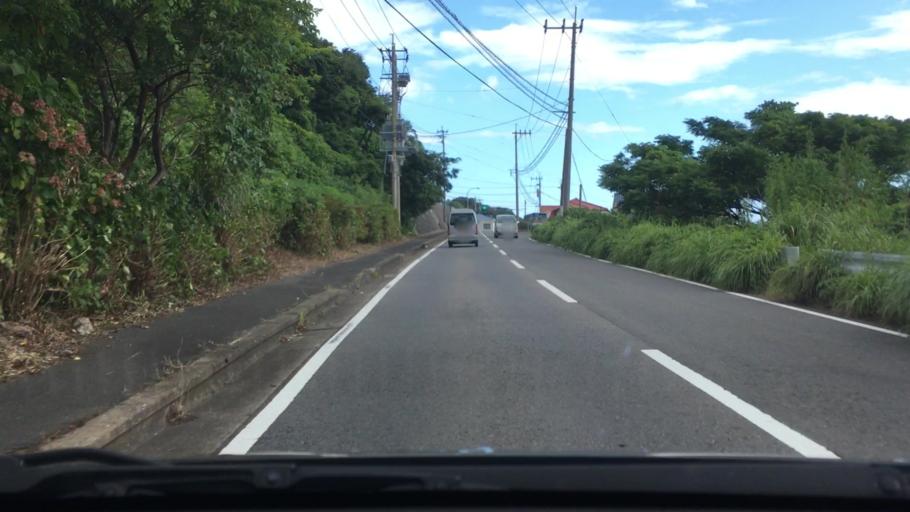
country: JP
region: Nagasaki
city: Togitsu
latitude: 32.8645
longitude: 129.6833
